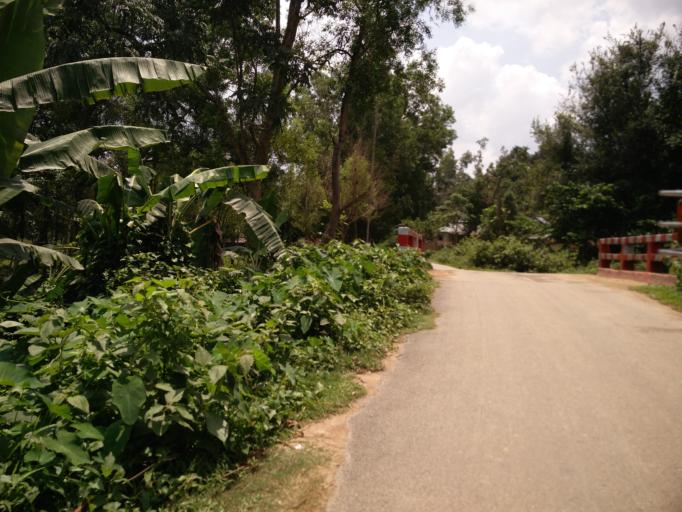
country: IN
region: Tripura
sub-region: Dhalai
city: Kamalpur
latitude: 24.3035
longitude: 91.7781
